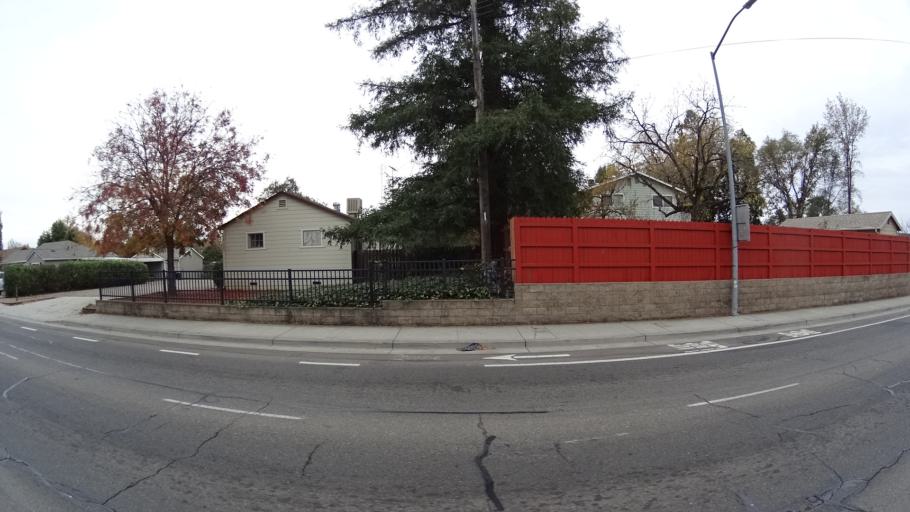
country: US
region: California
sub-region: Sacramento County
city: Citrus Heights
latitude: 38.7073
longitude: -121.3011
